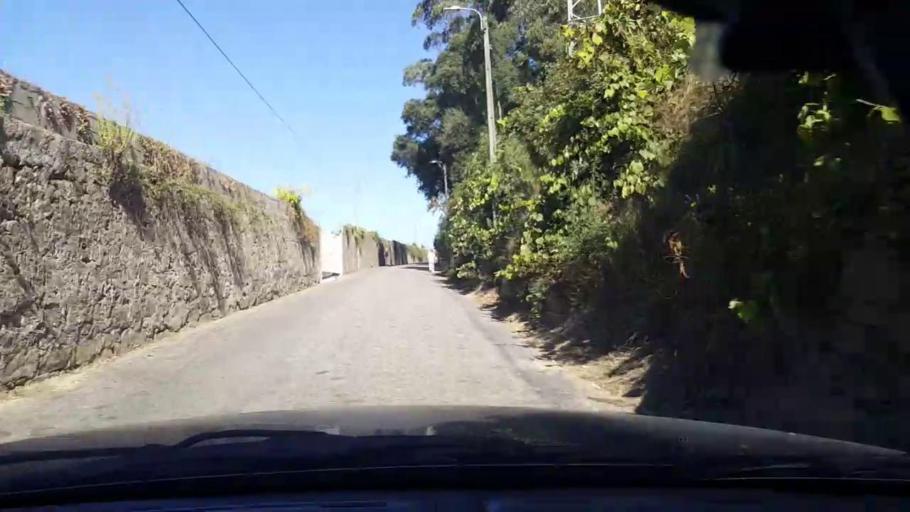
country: PT
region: Porto
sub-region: Maia
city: Gemunde
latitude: 41.2835
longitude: -8.6724
